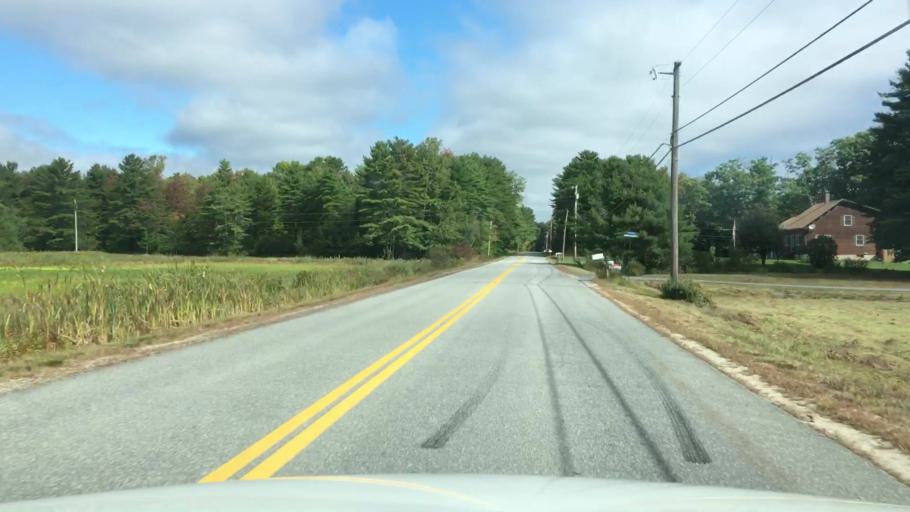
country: US
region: Maine
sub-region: Cumberland County
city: Brunswick
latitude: 43.9381
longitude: -69.9036
